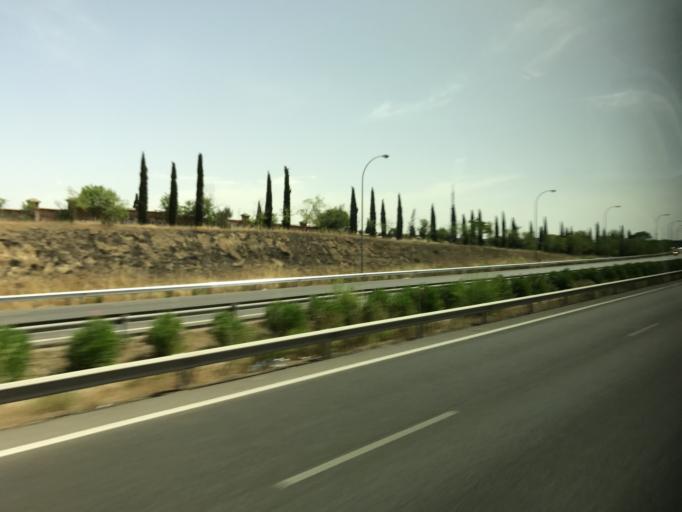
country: ES
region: Madrid
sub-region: Provincia de Madrid
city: Moratalaz
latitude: 40.4144
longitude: -3.6429
